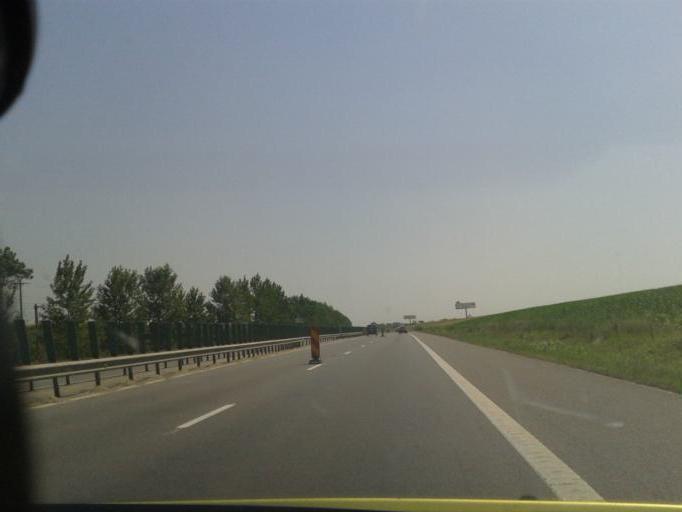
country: RO
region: Calarasi
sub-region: Comuna Tamadau Mare
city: Tamadau Mare
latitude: 44.4458
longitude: 26.5699
